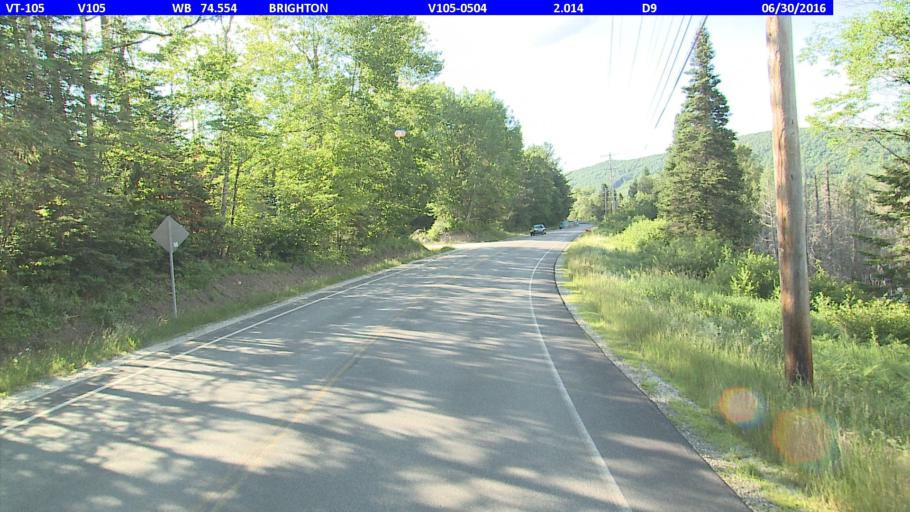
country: US
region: Vermont
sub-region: Caledonia County
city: Lyndonville
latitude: 44.7986
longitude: -71.9144
